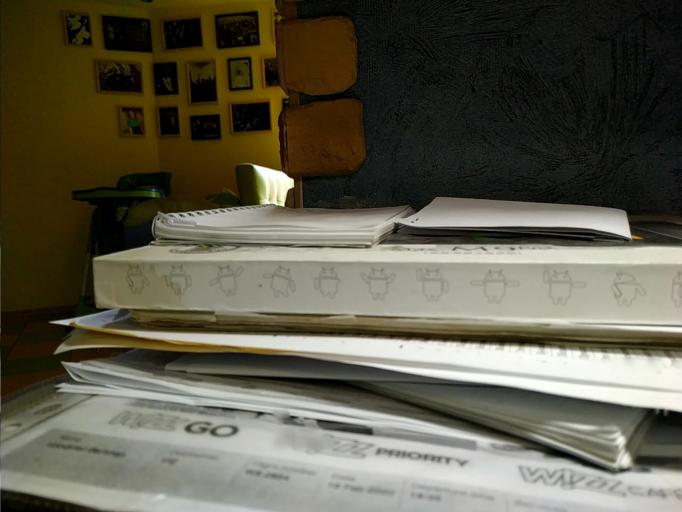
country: RU
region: Pskov
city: Plyussa
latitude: 58.6188
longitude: 29.3886
